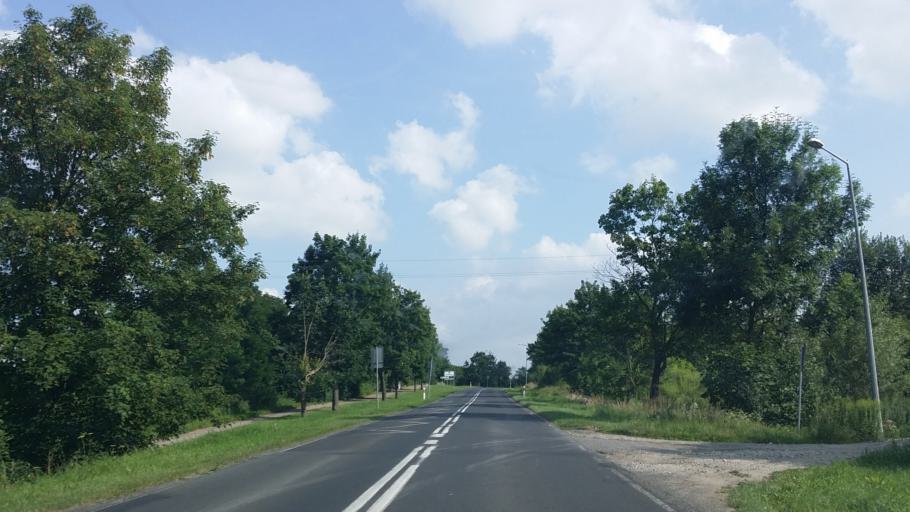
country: PL
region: Lubusz
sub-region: Powiat gorzowski
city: Klodawa
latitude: 52.7781
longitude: 15.2281
